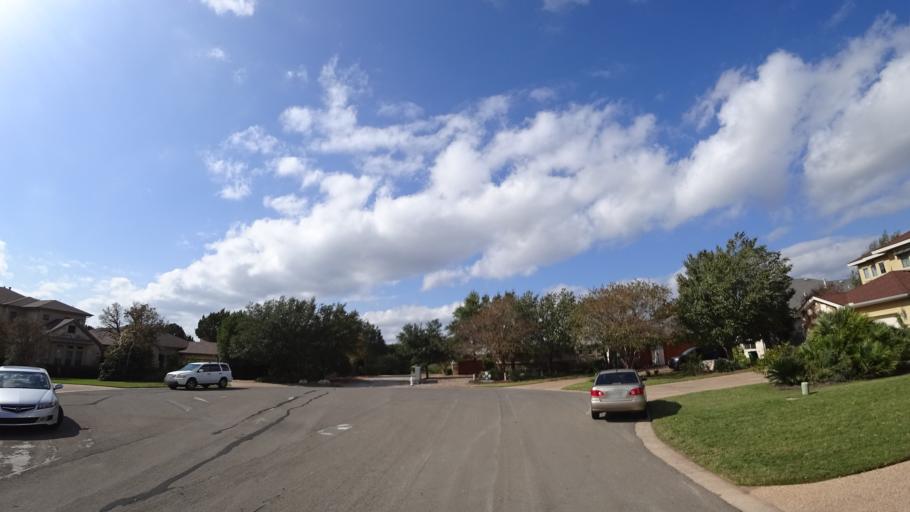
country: US
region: Texas
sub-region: Williamson County
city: Jollyville
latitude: 30.4225
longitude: -97.7908
